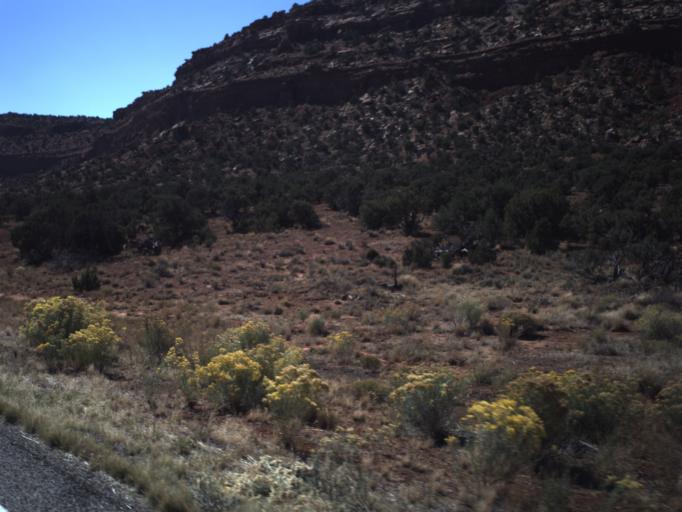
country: US
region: Utah
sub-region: San Juan County
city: Blanding
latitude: 37.6169
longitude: -110.0832
